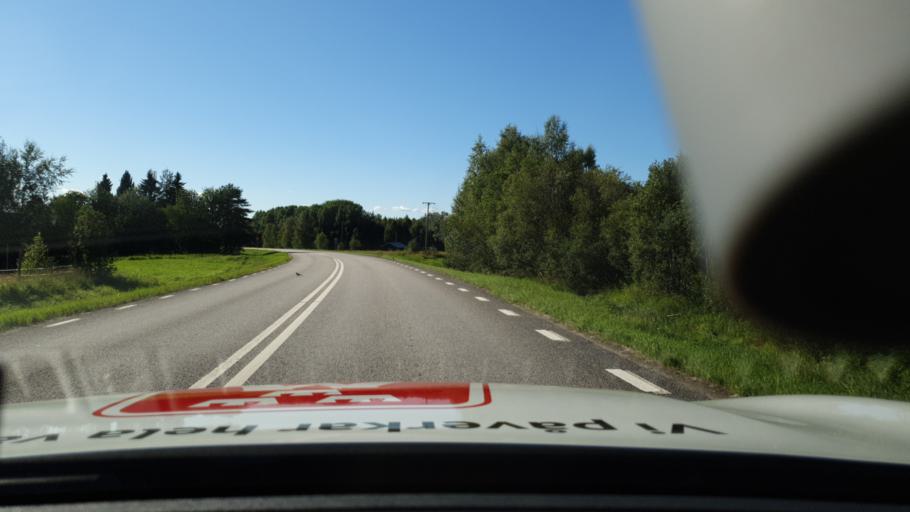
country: SE
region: Norrbotten
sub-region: Pitea Kommun
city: Rosvik
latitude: 65.5698
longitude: 21.7718
